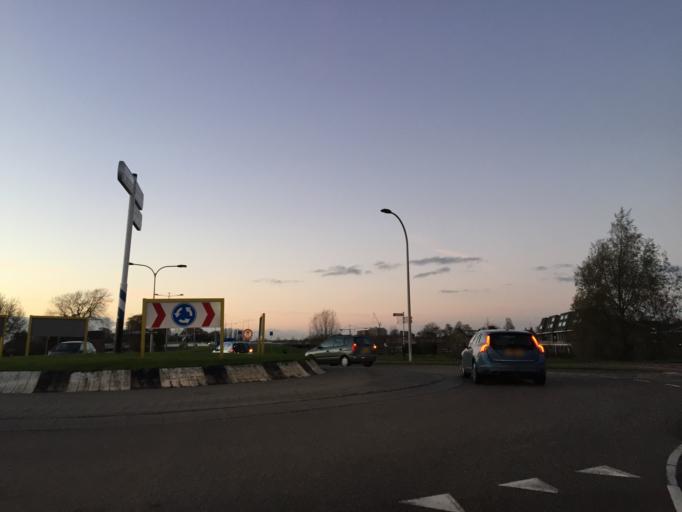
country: NL
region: South Holland
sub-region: Gemeente Lansingerland
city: Berkel en Rodenrijs
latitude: 51.9958
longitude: 4.4568
